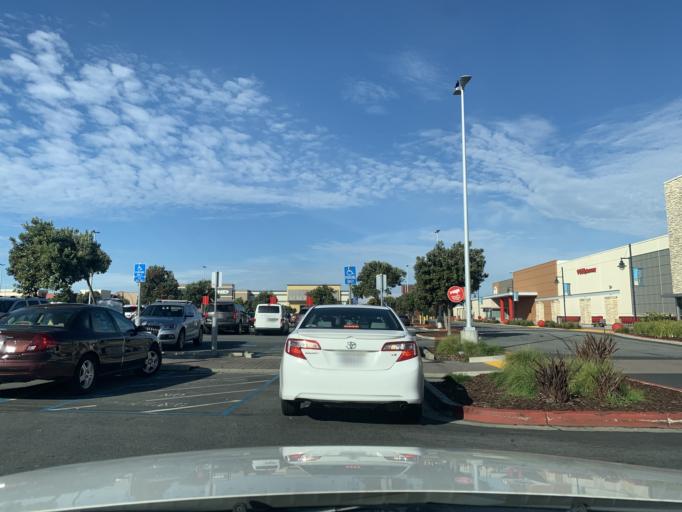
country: US
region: California
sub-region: Monterey County
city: Marina
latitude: 36.6670
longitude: -121.8103
